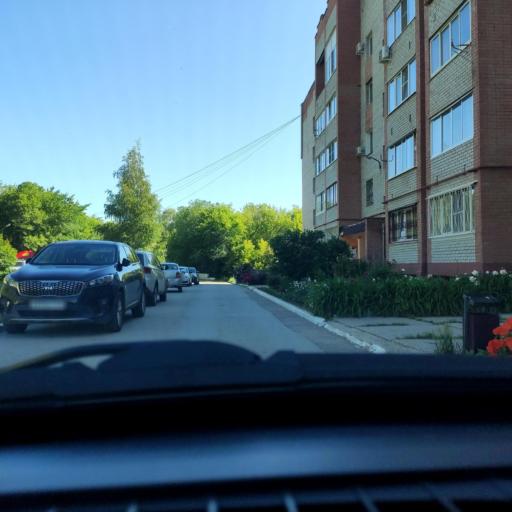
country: RU
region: Samara
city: Zhigulevsk
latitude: 53.4068
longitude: 49.4717
